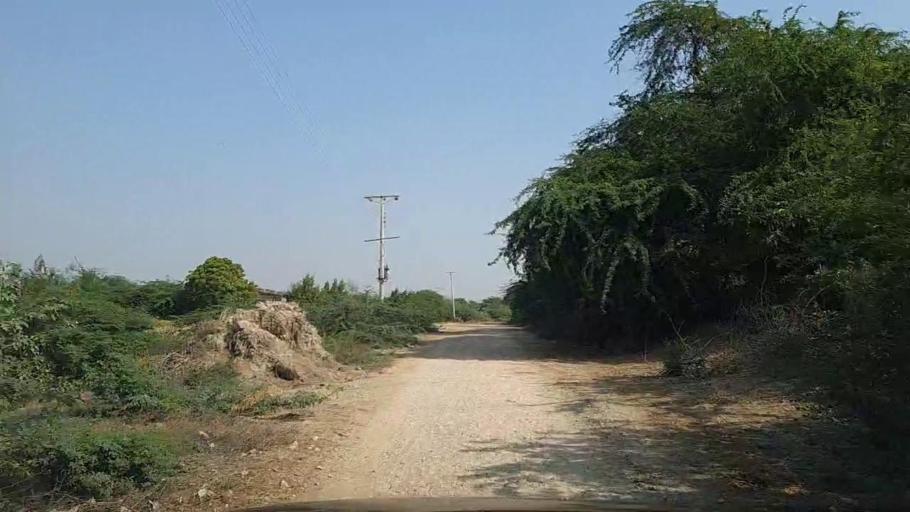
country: PK
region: Sindh
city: Thatta
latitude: 24.7702
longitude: 67.7777
